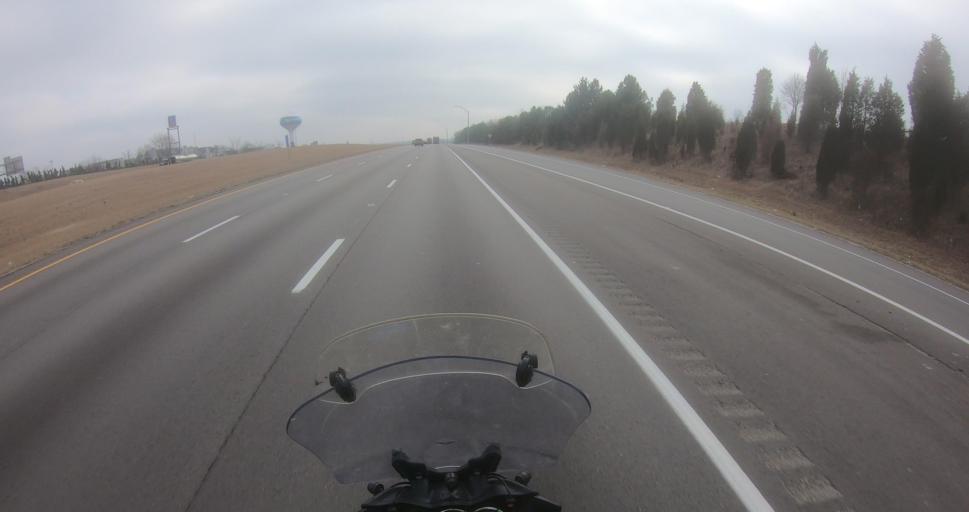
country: US
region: Ohio
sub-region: Montgomery County
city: West Carrollton City
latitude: 39.6360
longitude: -84.2313
